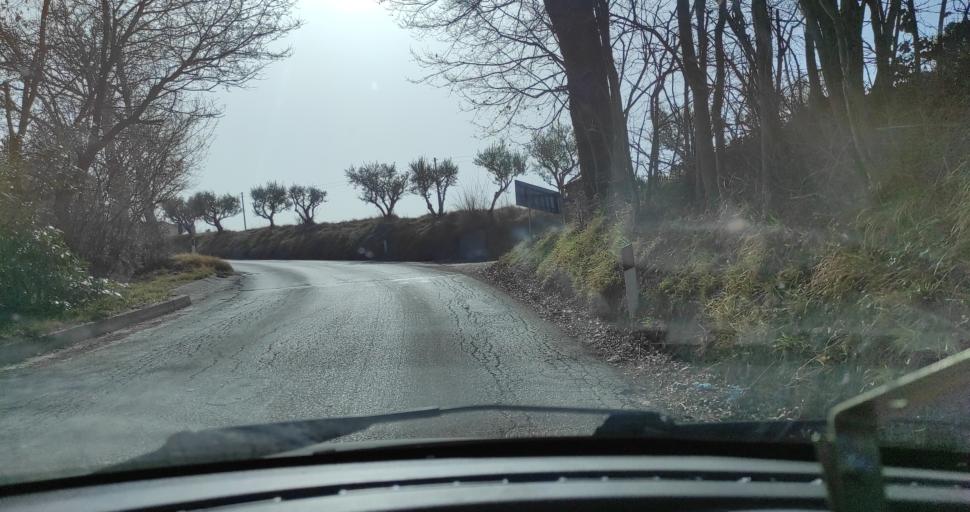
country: IT
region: The Marches
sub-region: Provincia di Macerata
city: Loro Piceno
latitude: 43.1660
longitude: 13.4052
